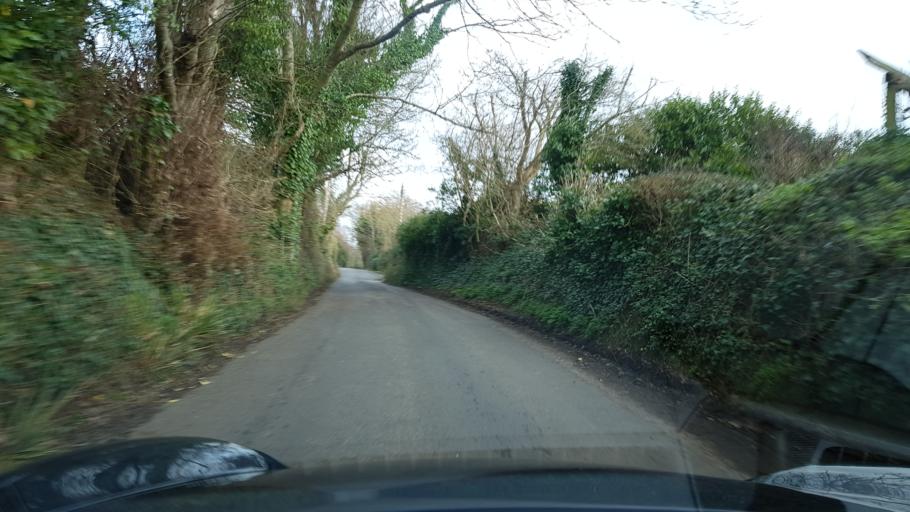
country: GB
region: England
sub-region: Dorset
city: Bridport
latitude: 50.7062
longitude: -2.7259
